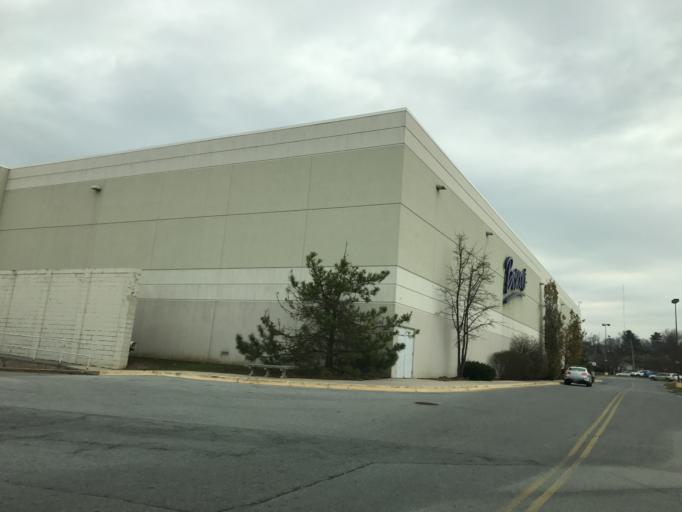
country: US
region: Maryland
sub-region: Frederick County
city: Braddock Heights
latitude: 39.4216
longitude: -77.4596
